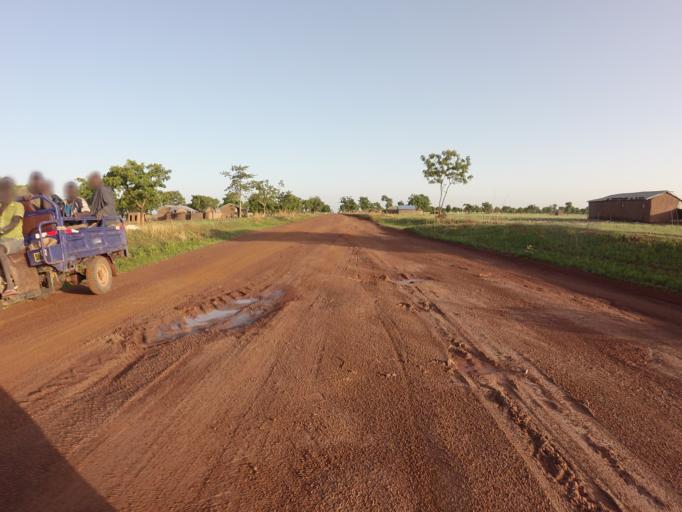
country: TG
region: Savanes
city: Sansanne-Mango
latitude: 10.2675
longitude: -0.0810
